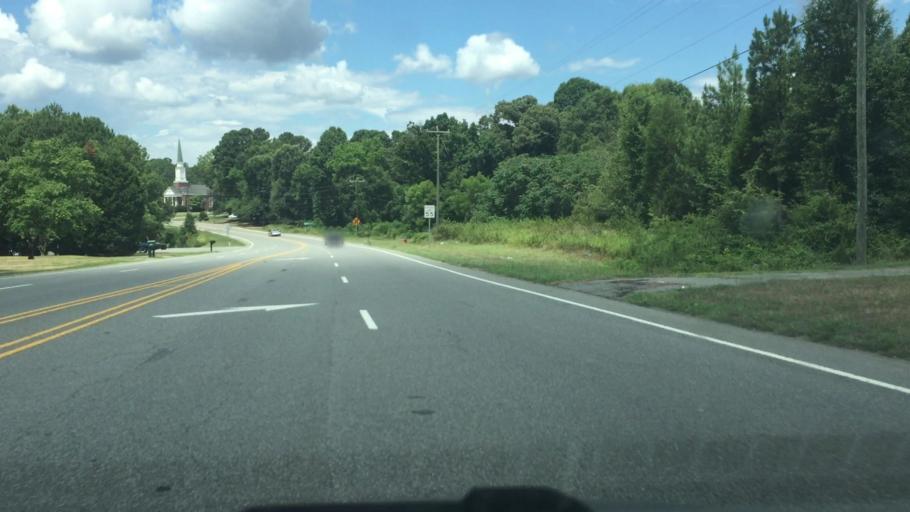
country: US
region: North Carolina
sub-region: Rowan County
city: Enochville
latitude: 35.4907
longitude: -80.6743
